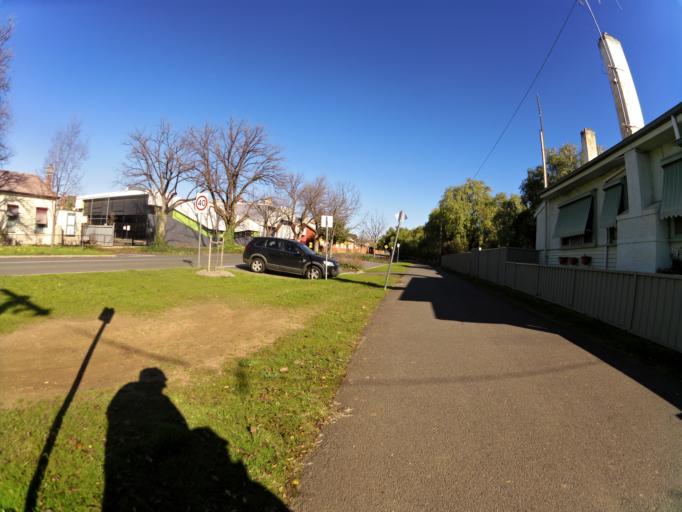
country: AU
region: Victoria
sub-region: Greater Bendigo
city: Bendigo
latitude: -36.7533
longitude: 144.2850
